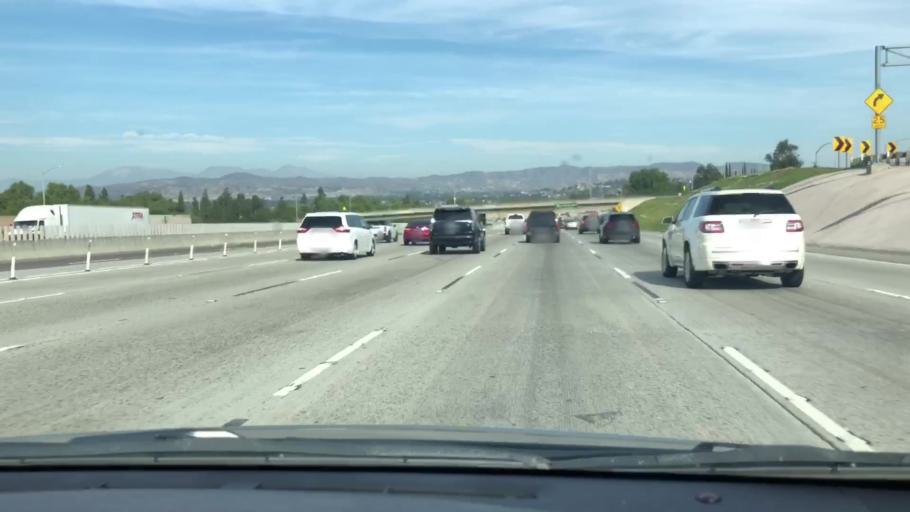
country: US
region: California
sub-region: Orange County
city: Villa Park
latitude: 33.8502
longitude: -117.8158
